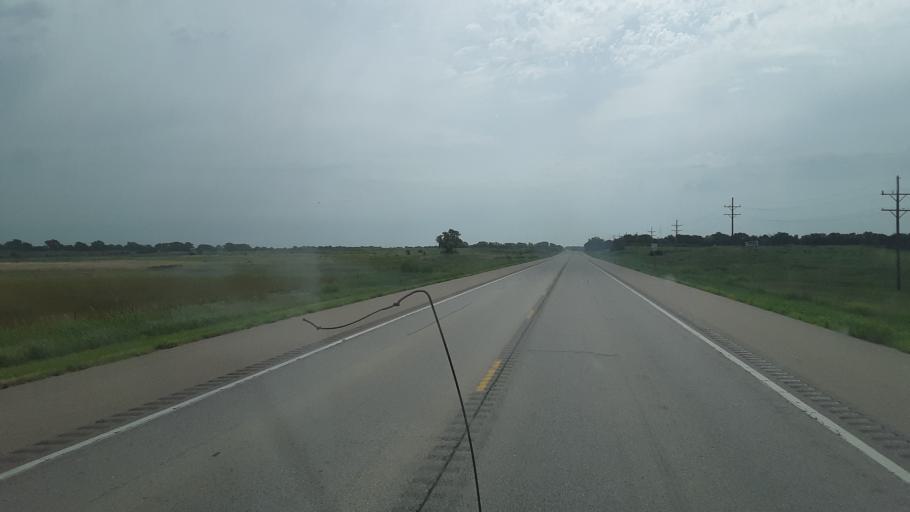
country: US
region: Kansas
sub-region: Stafford County
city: Stafford
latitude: 37.9551
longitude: -98.4707
